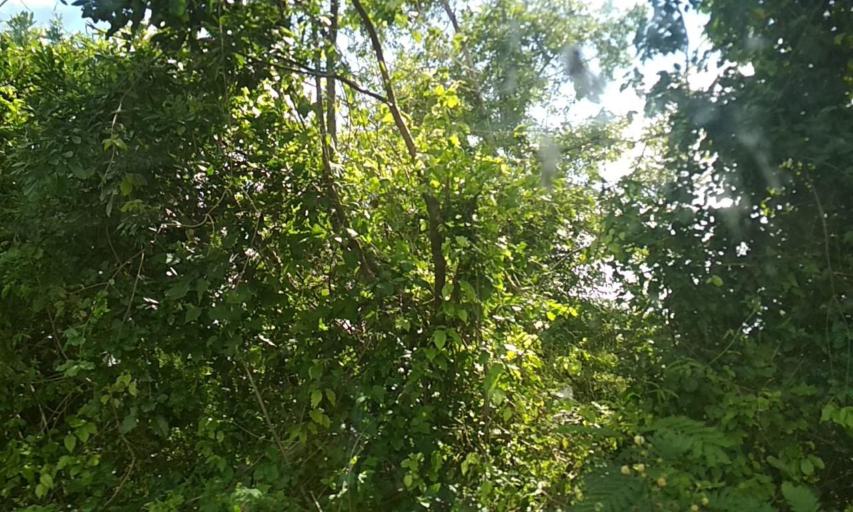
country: MX
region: Puebla
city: San Jose Acateno
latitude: 20.2827
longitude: -97.1303
